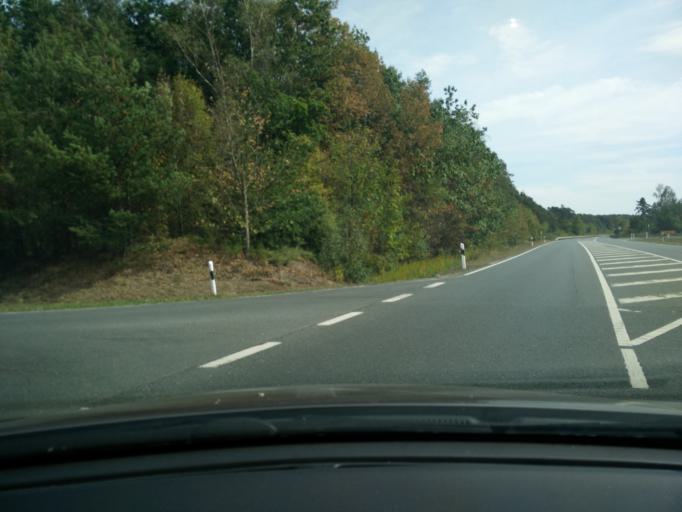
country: DE
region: Bavaria
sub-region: Regierungsbezirk Mittelfranken
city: Emskirchen
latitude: 49.5658
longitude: 10.6812
